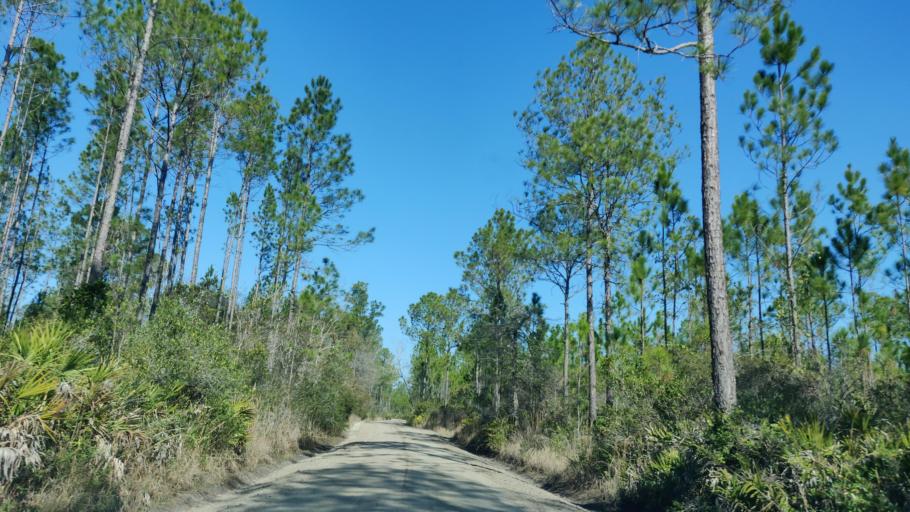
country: US
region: Florida
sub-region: Clay County
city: Middleburg
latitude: 30.1669
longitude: -81.9501
